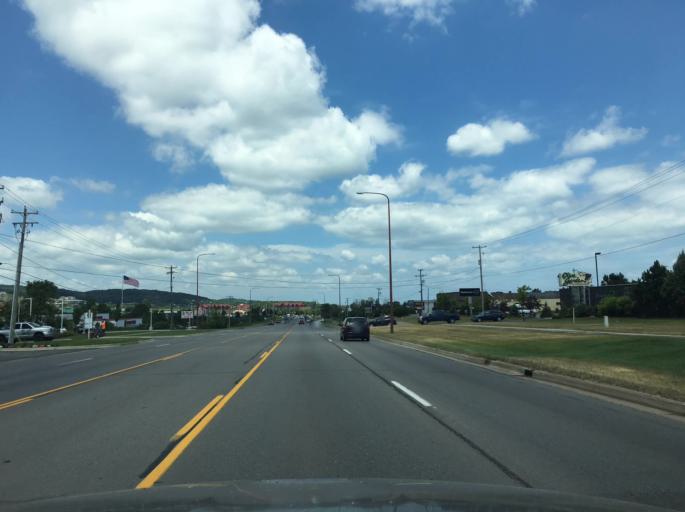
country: US
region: Michigan
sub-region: Grand Traverse County
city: Traverse City
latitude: 44.7281
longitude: -85.6461
